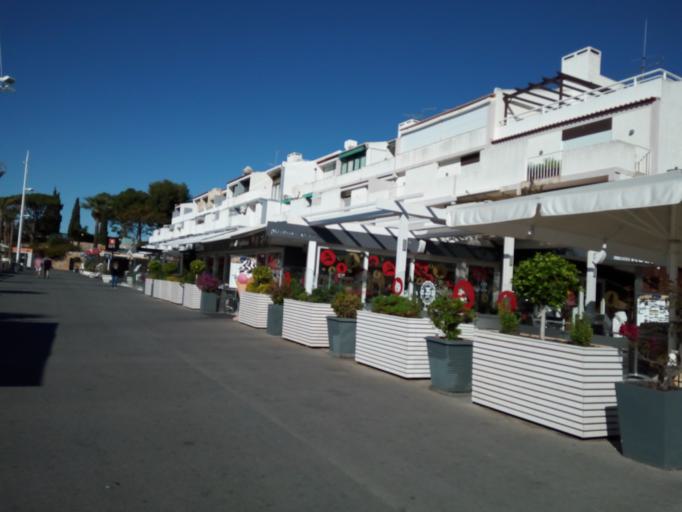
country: PT
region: Faro
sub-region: Loule
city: Vilamoura
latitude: 37.0787
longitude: -8.1189
